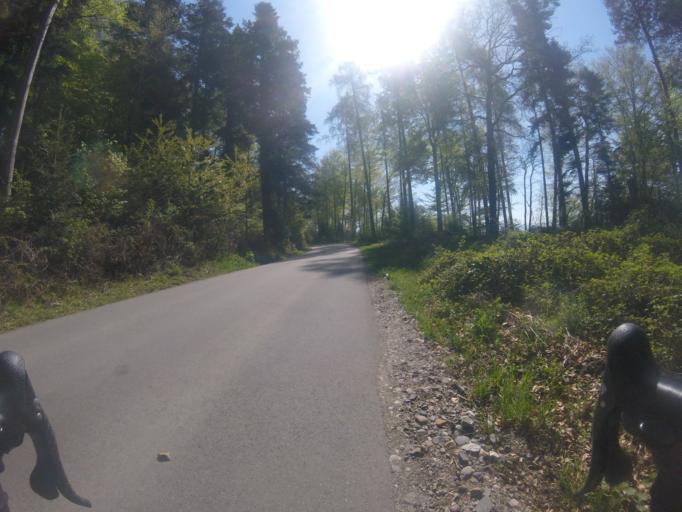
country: CH
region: Bern
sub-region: Bern-Mittelland District
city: Laupen
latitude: 46.9013
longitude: 7.2534
